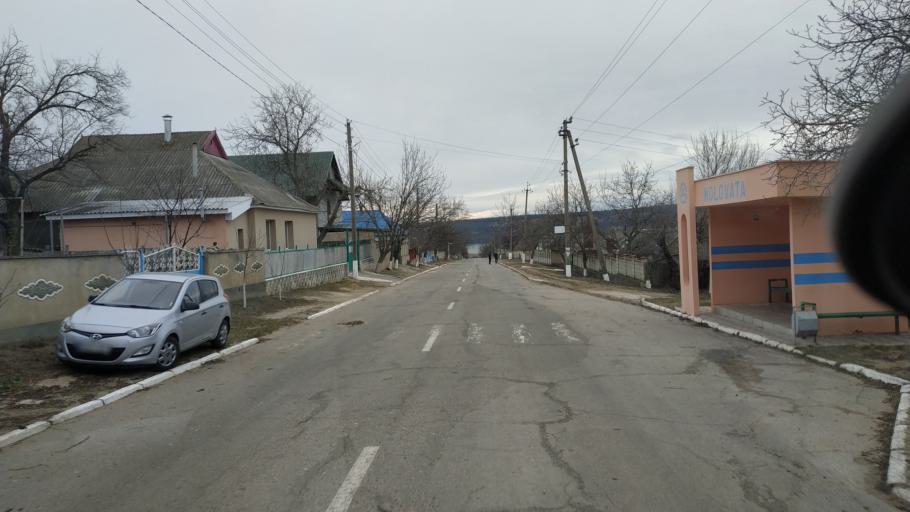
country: MD
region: Telenesti
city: Cocieri
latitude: 47.3483
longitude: 29.1175
